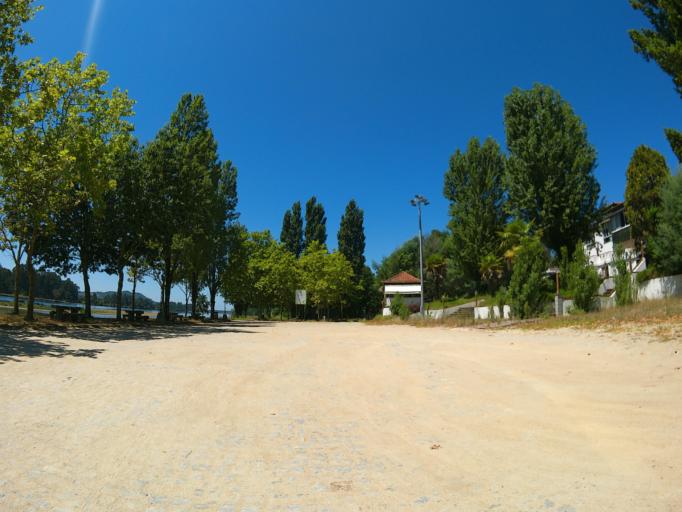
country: PT
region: Viana do Castelo
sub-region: Viana do Castelo
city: Darque
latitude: 41.7014
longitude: -8.7487
